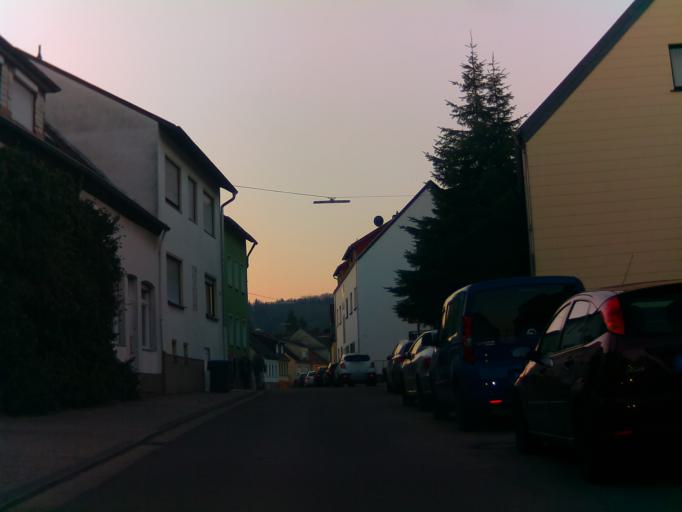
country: DE
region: Saarland
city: Sulzbach
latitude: 49.2727
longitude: 7.0359
